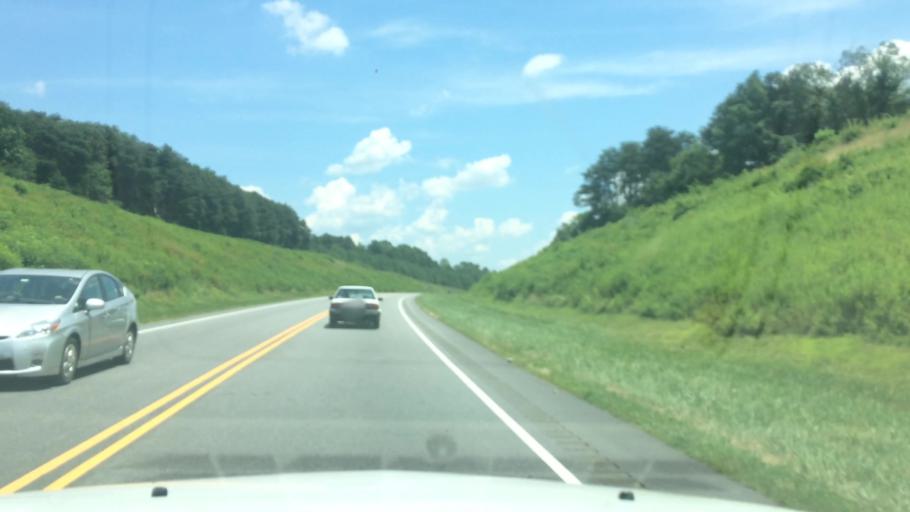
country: US
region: North Carolina
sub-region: Alexander County
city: Taylorsville
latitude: 35.9121
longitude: -81.1521
